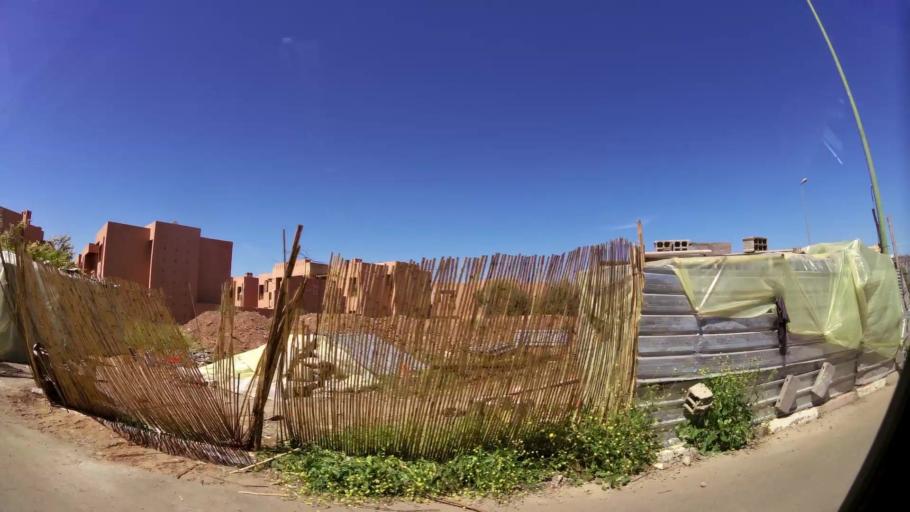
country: MA
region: Marrakech-Tensift-Al Haouz
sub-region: Marrakech
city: Marrakesh
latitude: 31.5712
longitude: -7.9848
